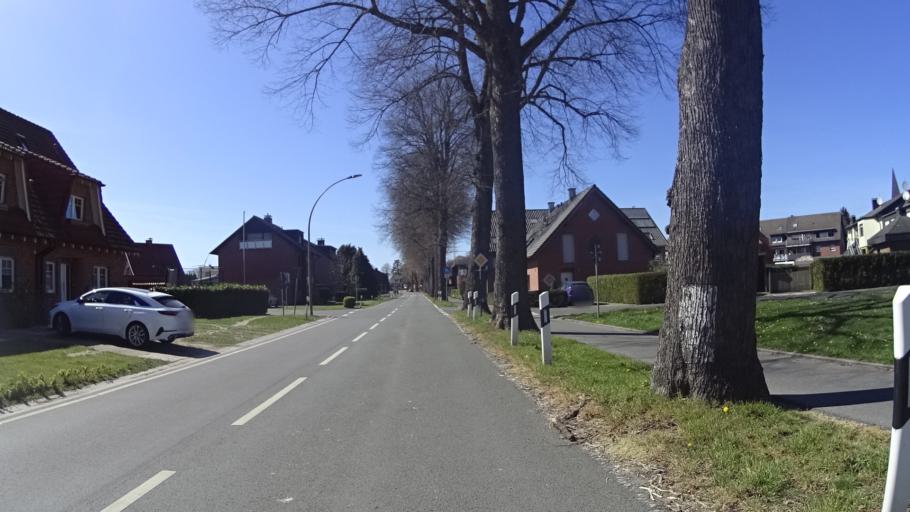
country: DE
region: North Rhine-Westphalia
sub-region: Regierungsbezirk Munster
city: Haltern
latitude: 51.7719
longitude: 7.2260
